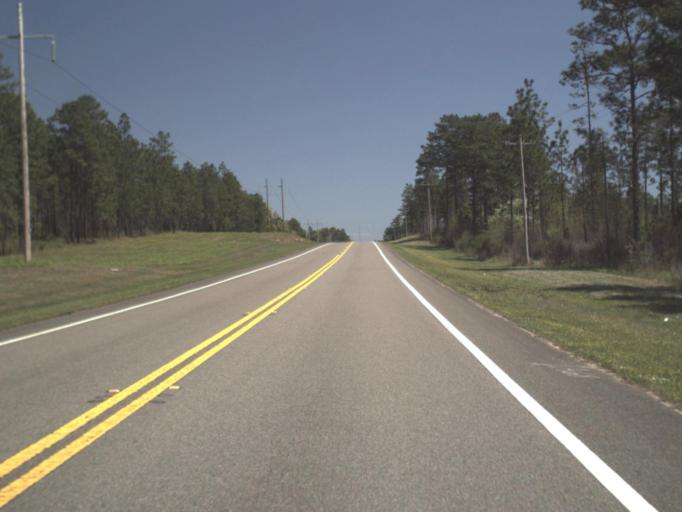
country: US
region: Florida
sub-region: Santa Rosa County
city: Point Baker
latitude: 30.8678
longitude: -86.9200
